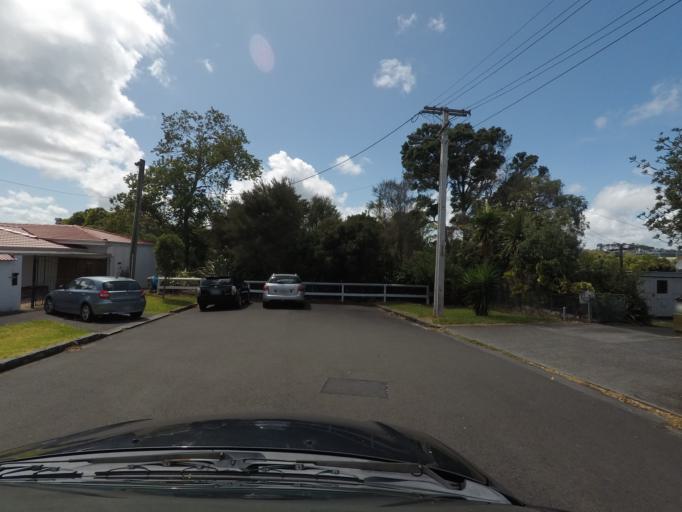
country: NZ
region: Auckland
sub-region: Auckland
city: Rosebank
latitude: -36.8600
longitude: 174.7100
